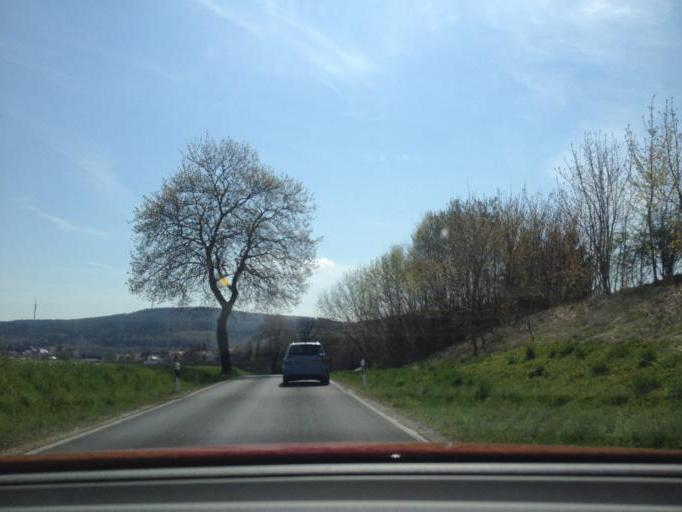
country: DE
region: Bavaria
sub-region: Upper Franconia
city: Arzberg
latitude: 50.0601
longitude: 12.1695
